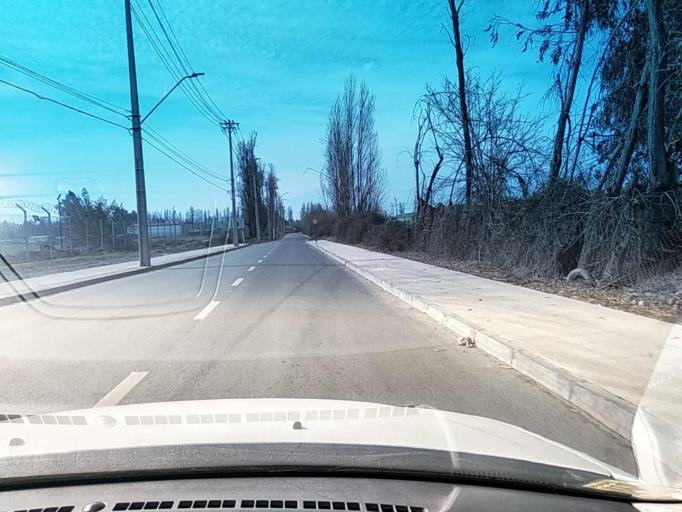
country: CL
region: Santiago Metropolitan
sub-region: Provincia de Chacabuco
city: Chicureo Abajo
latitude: -33.2861
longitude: -70.7320
